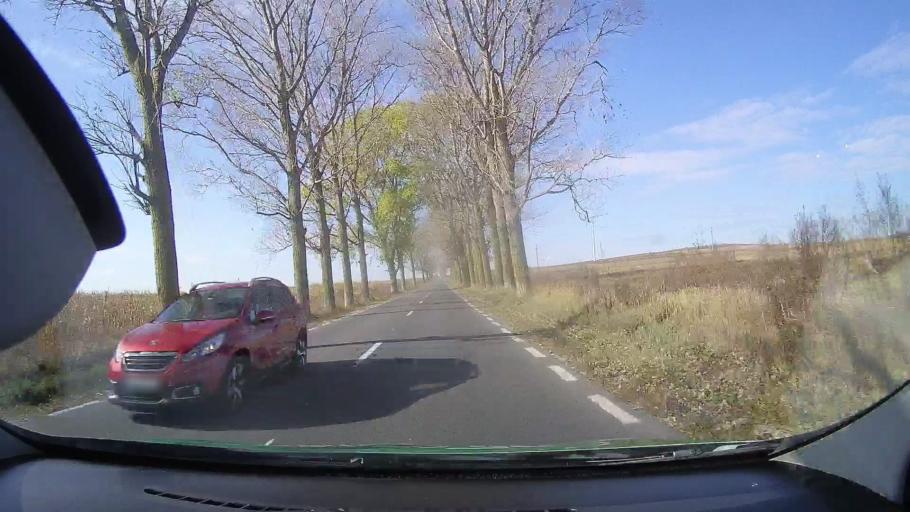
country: RO
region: Tulcea
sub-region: Comuna Valea Nucarilor
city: Iazurile
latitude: 45.0259
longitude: 28.9951
